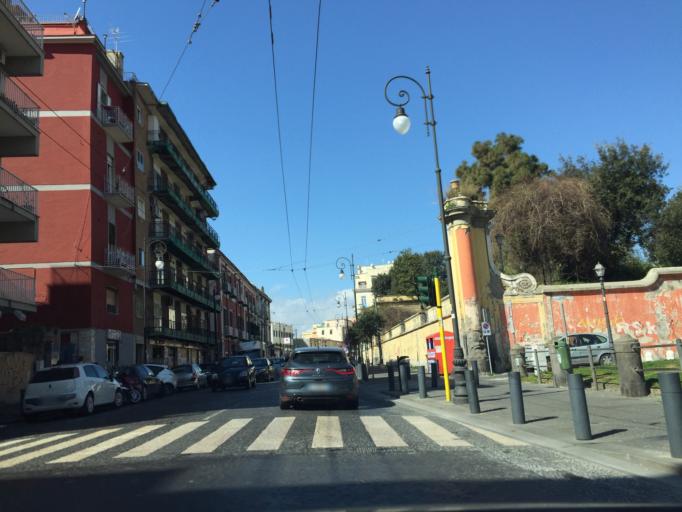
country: IT
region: Campania
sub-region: Provincia di Napoli
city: Portici
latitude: 40.8181
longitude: 14.3307
